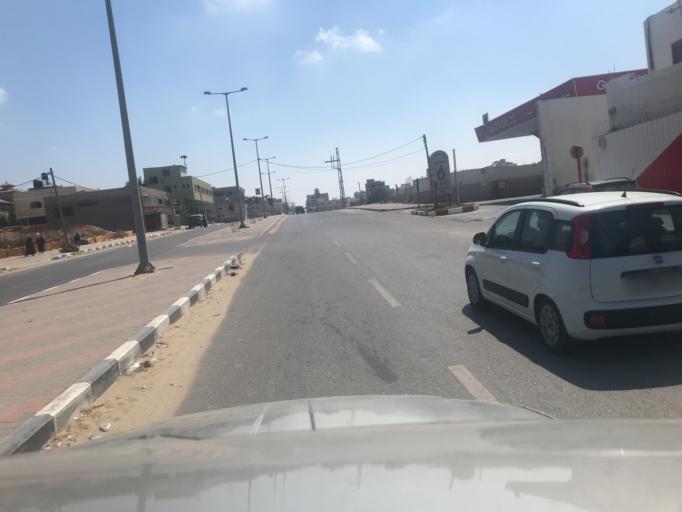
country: PS
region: Gaza Strip
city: Bayt Lahya
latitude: 31.5535
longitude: 34.4683
